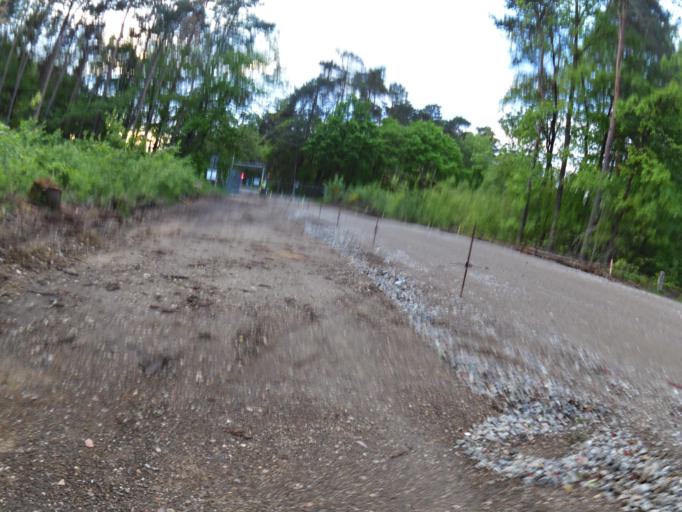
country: BE
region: Flanders
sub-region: Provincie Limburg
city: Genk
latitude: 50.9572
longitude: 5.5241
